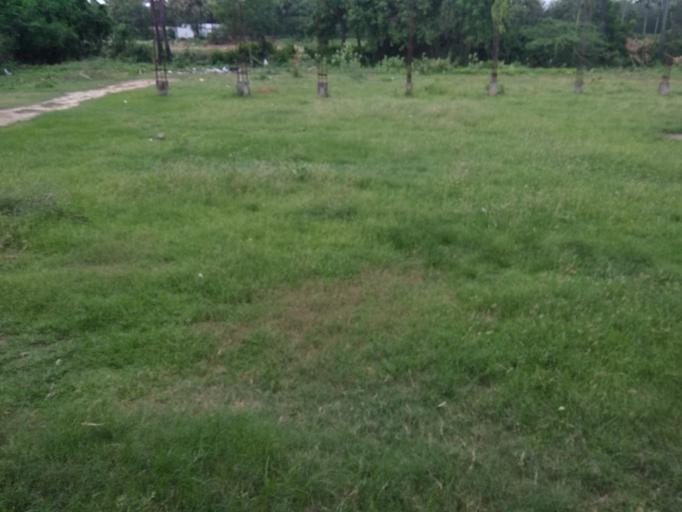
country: IN
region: Andhra Pradesh
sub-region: East Godavari
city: Ramanayyapeta
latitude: 16.8569
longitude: 82.2336
